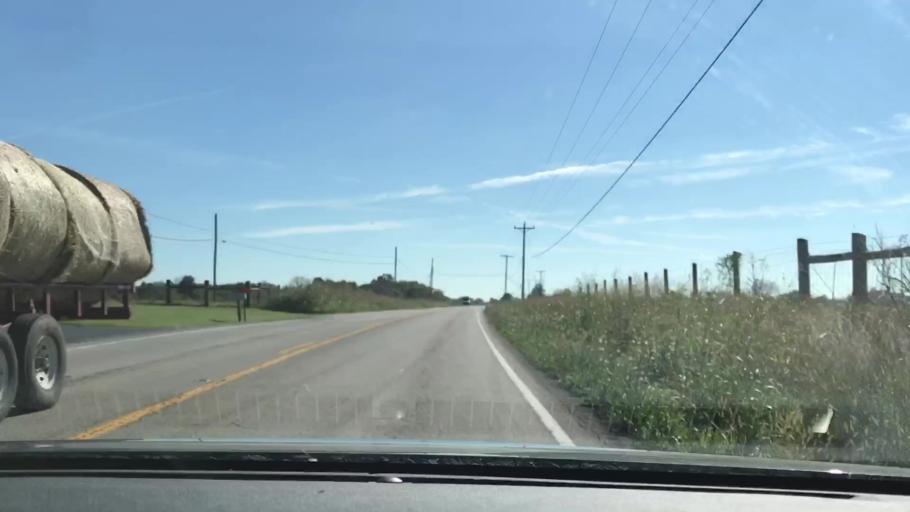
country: US
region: Kentucky
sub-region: Christian County
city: Hopkinsville
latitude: 36.8603
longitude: -87.4337
